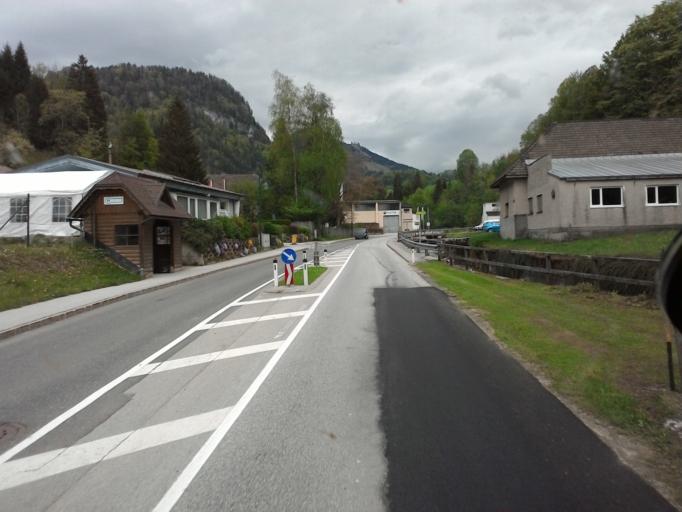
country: AT
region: Upper Austria
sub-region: Politischer Bezirk Kirchdorf an der Krems
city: Rossleithen
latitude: 47.7129
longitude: 14.3935
